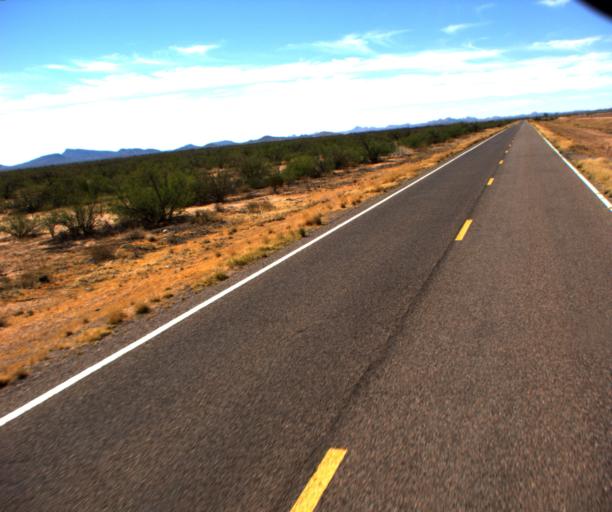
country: US
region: Arizona
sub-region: Yavapai County
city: Congress
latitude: 33.9615
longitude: -113.1416
